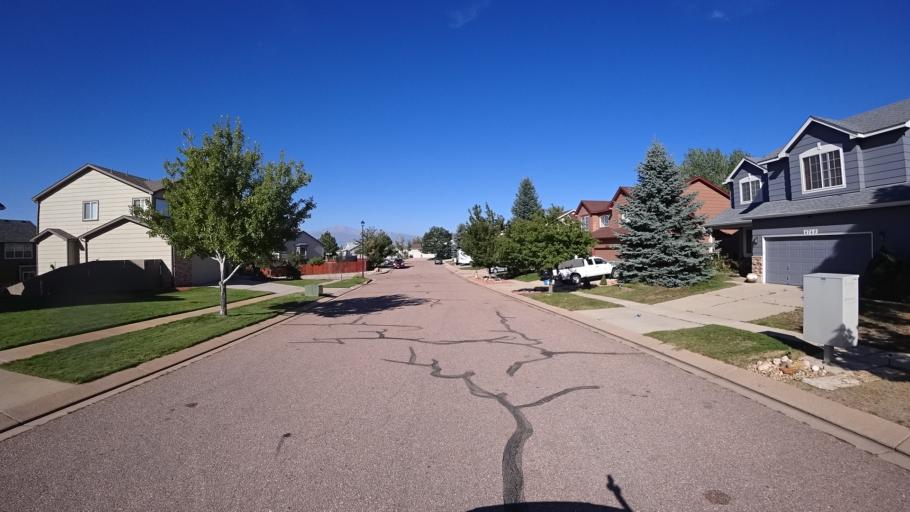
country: US
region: Colorado
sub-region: El Paso County
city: Black Forest
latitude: 38.9457
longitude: -104.7397
